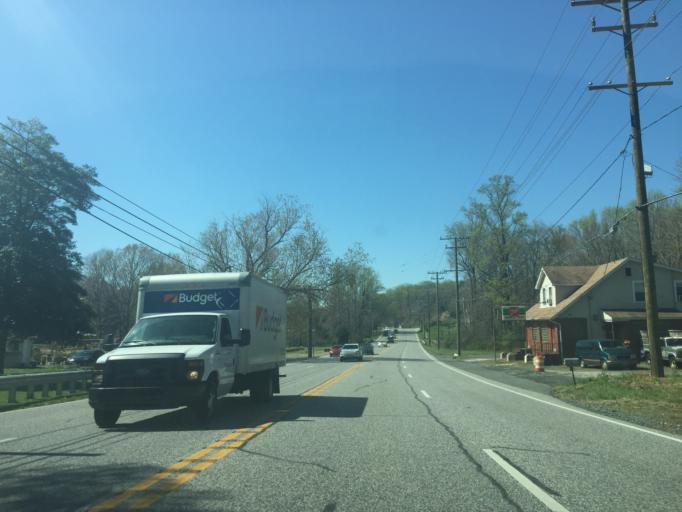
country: US
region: Maryland
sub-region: Baltimore County
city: Kingsville
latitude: 39.4647
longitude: -76.4113
